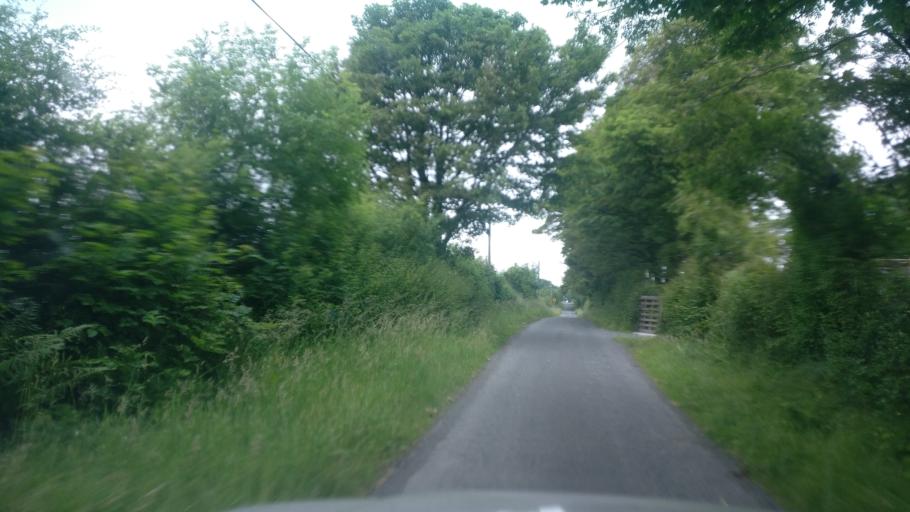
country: IE
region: Connaught
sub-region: County Galway
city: Ballinasloe
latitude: 53.3026
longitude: -8.3616
